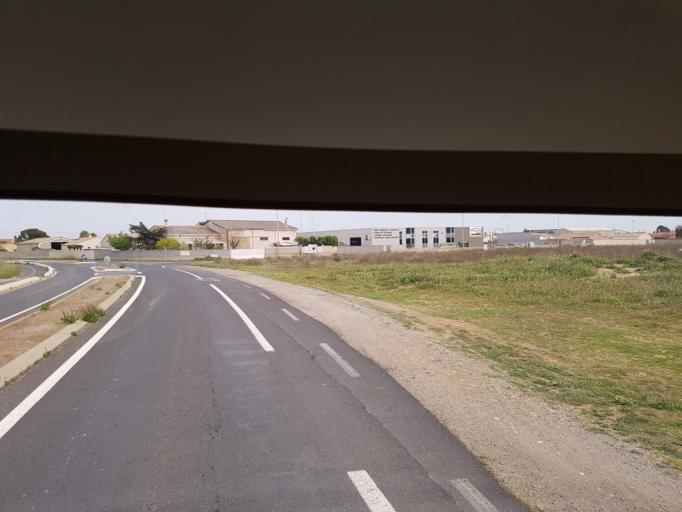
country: FR
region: Languedoc-Roussillon
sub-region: Departement de l'Herault
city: Vendres
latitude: 43.2702
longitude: 3.2372
